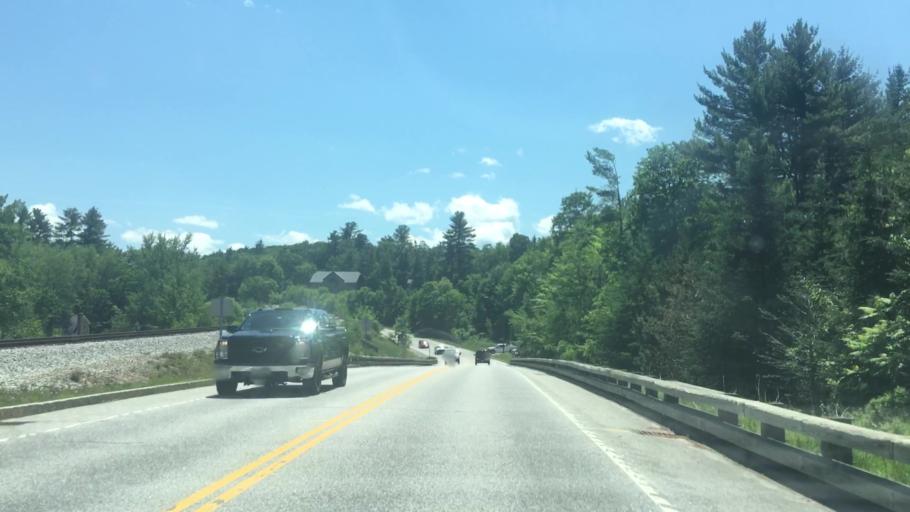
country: US
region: New Hampshire
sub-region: Carroll County
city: North Conway
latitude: 44.0463
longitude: -71.1227
